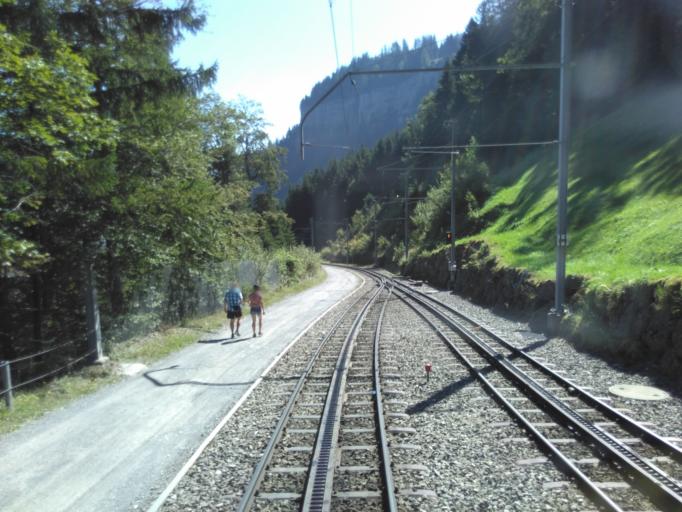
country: CH
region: Schwyz
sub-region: Bezirk Schwyz
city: Arth
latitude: 47.0383
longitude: 8.5054
